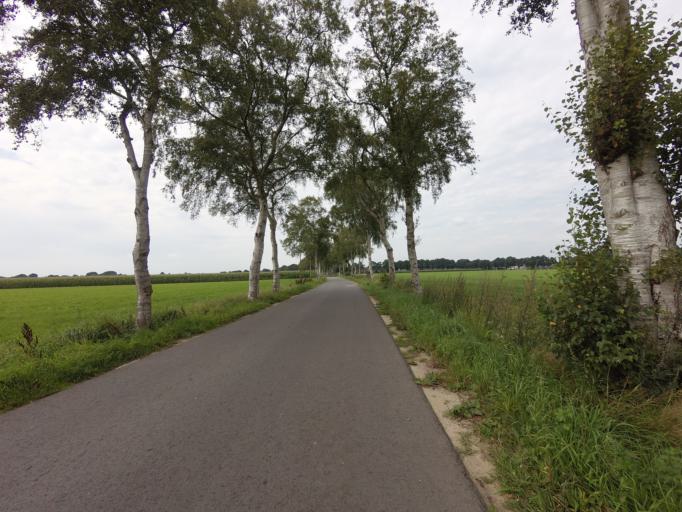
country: NL
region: Drenthe
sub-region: Gemeente Westerveld
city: Dwingeloo
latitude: 52.8289
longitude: 6.3823
